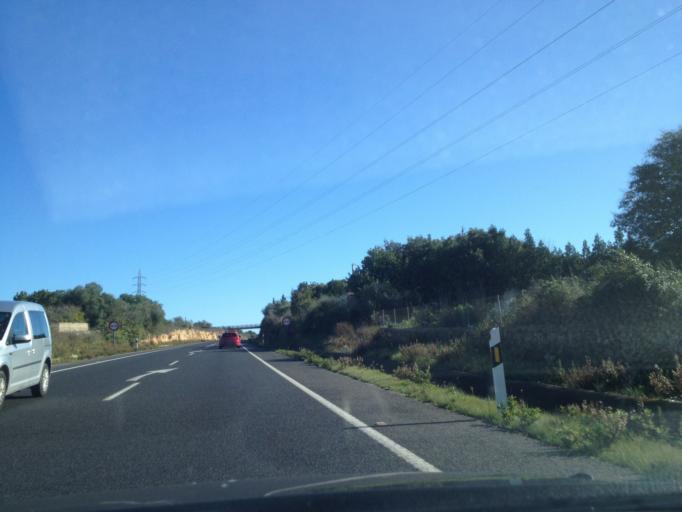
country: ES
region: Balearic Islands
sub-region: Illes Balears
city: Manacor
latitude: 39.5852
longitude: 3.2117
